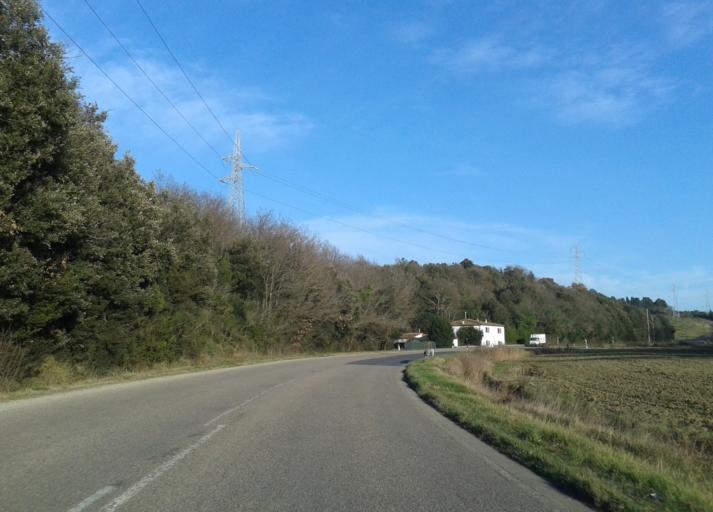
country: IT
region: Tuscany
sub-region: Provincia di Livorno
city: Guasticce
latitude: 43.5699
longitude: 10.4051
